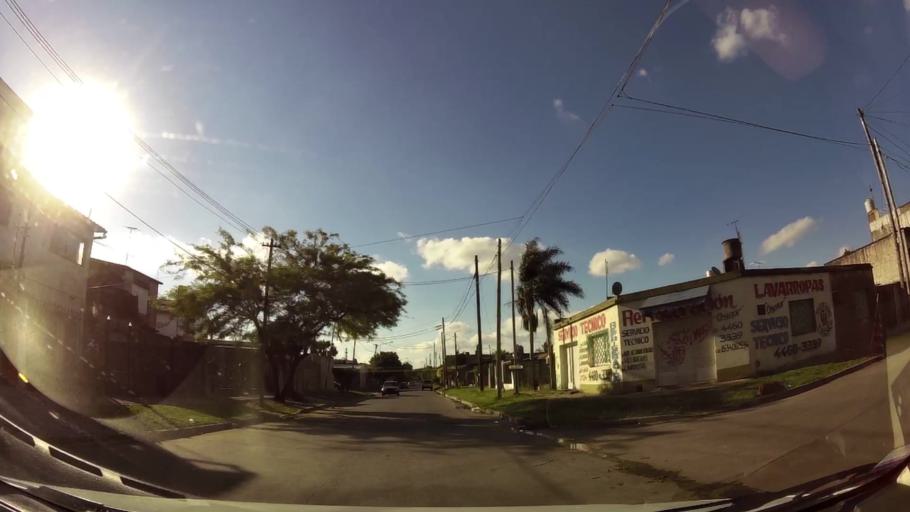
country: AR
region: Buenos Aires
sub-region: Partido de Moron
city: Moron
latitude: -34.6796
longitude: -58.6104
